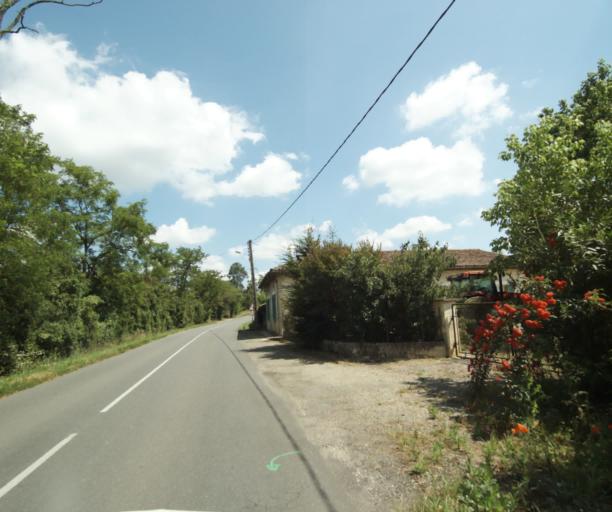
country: FR
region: Midi-Pyrenees
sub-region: Departement du Tarn-et-Garonne
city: Montauban
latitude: 44.0712
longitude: 1.3671
